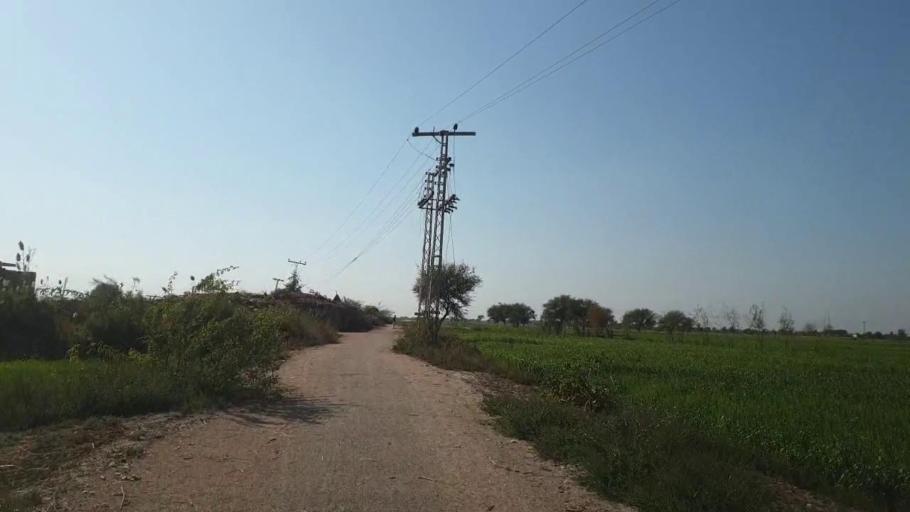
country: PK
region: Sindh
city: Mirpur Khas
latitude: 25.6335
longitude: 69.0432
